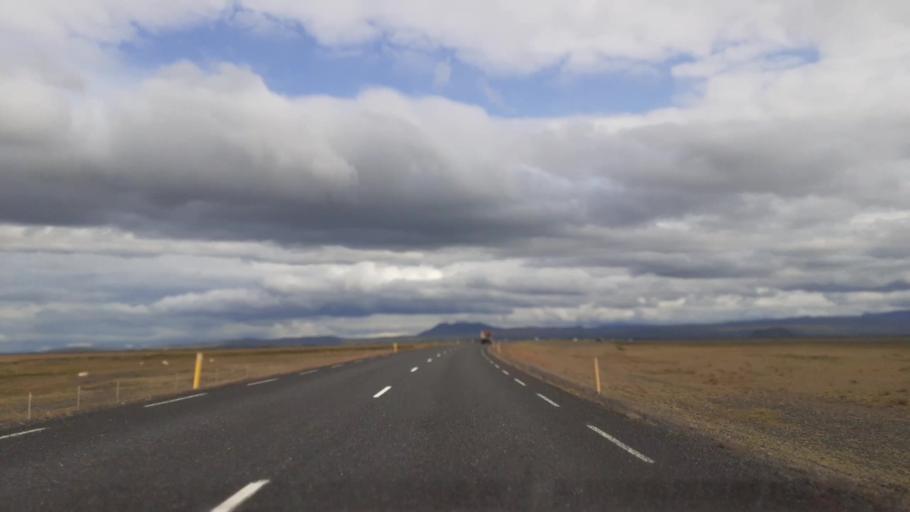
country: IS
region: South
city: Vestmannaeyjar
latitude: 63.6029
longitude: -20.0537
